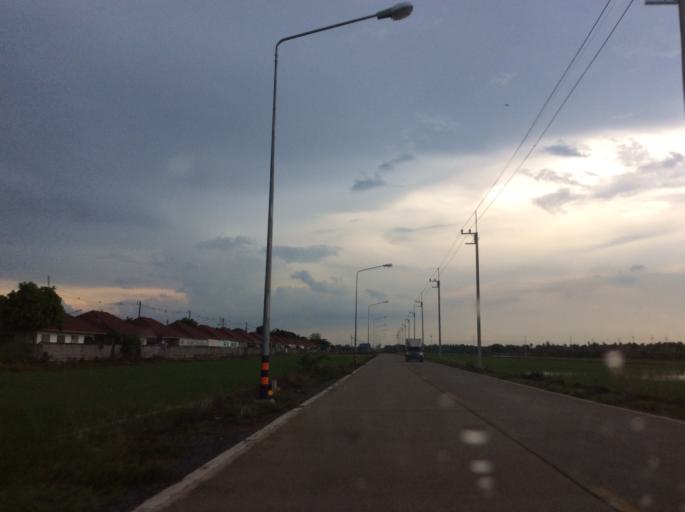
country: TH
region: Pathum Thani
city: Thanyaburi
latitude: 14.0031
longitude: 100.7444
